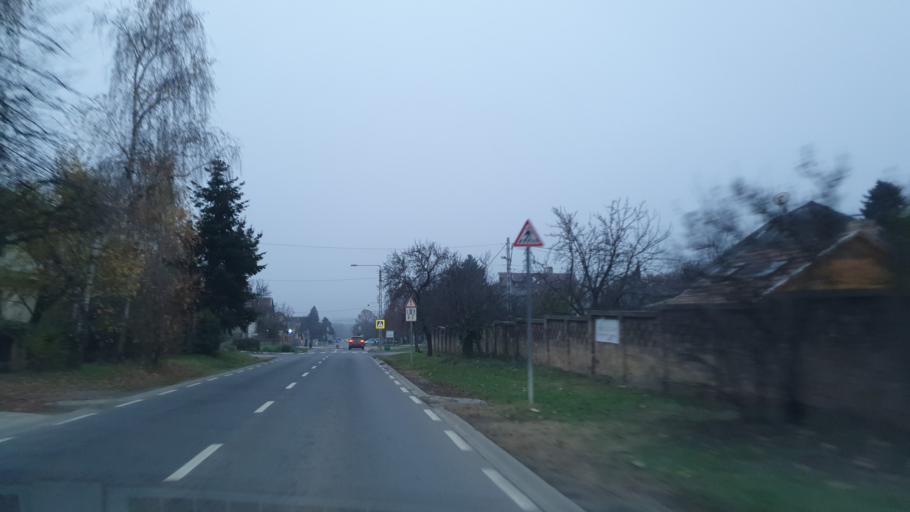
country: HU
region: Pest
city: Csomor
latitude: 47.5412
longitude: 19.2248
